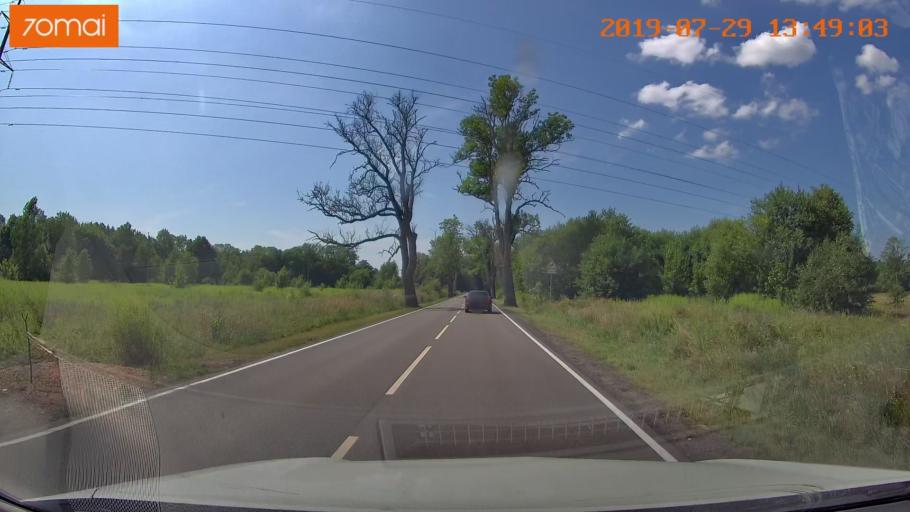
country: RU
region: Kaliningrad
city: Primorsk
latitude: 54.7357
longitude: 20.0303
